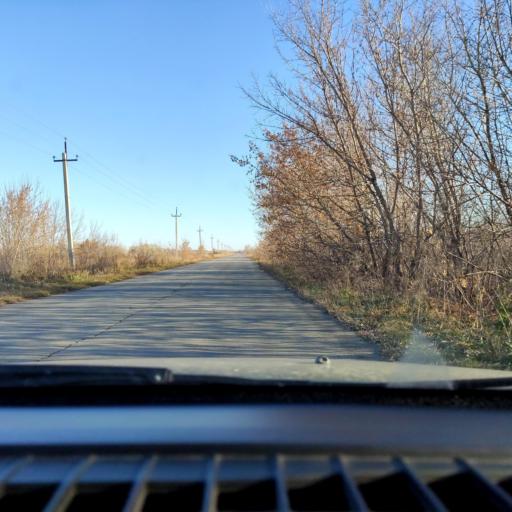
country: RU
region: Samara
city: Tol'yatti
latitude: 53.6492
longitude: 49.3210
